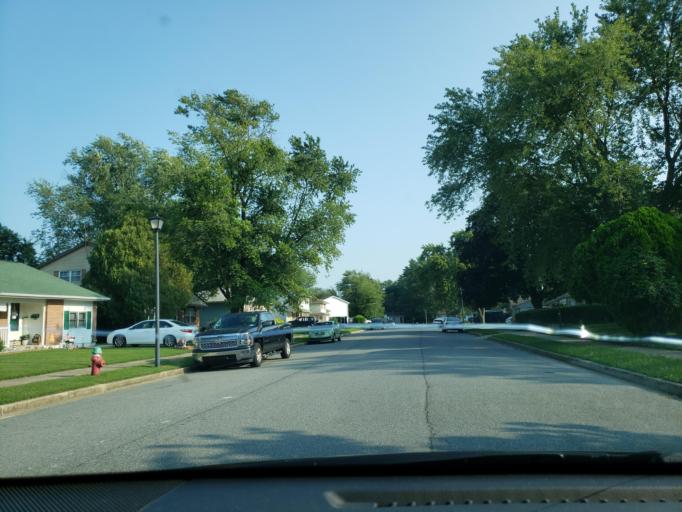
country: US
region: Delaware
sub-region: Kent County
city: Rodney Village
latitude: 39.1343
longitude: -75.5337
